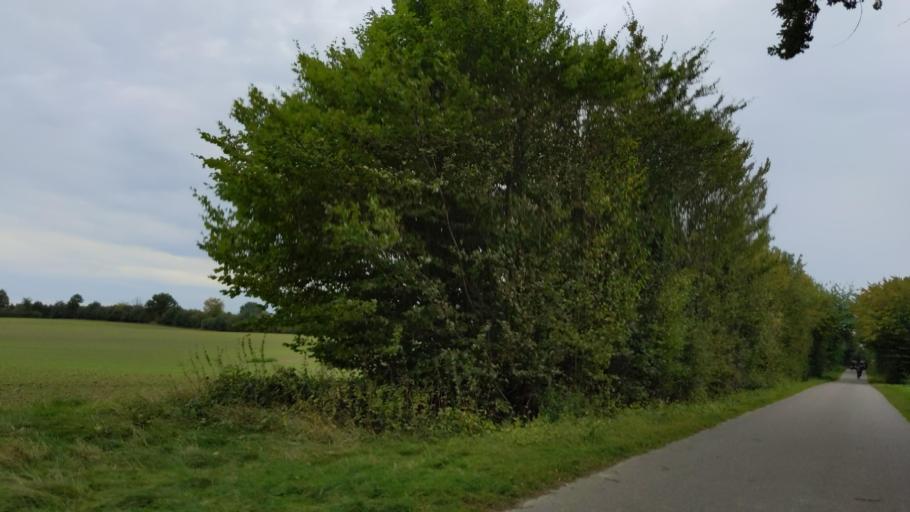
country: DE
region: Schleswig-Holstein
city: Bak
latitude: 53.7231
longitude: 10.7829
